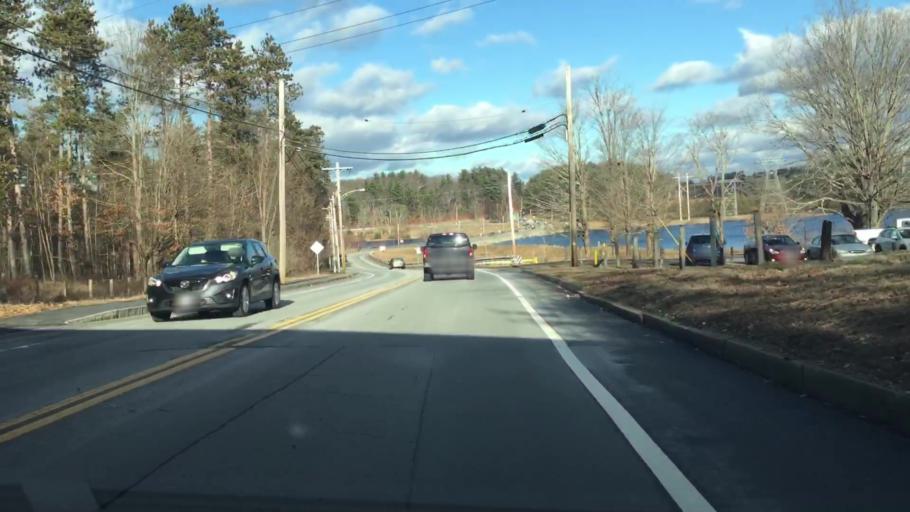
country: US
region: Massachusetts
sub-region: Worcester County
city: West Boylston
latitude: 42.3697
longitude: -71.7823
